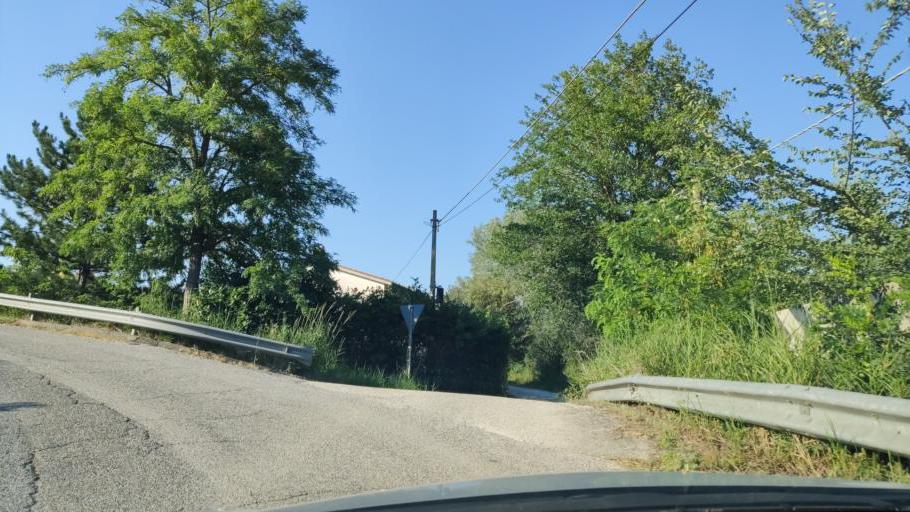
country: IT
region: Latium
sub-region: Provincia di Viterbo
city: Orte Scalo
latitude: 42.4720
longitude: 12.4330
